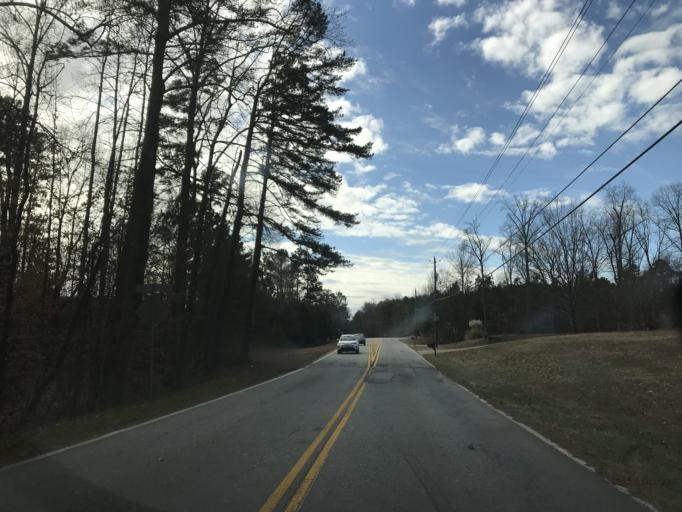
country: US
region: Georgia
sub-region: Douglas County
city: Douglasville
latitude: 33.7915
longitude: -84.7769
